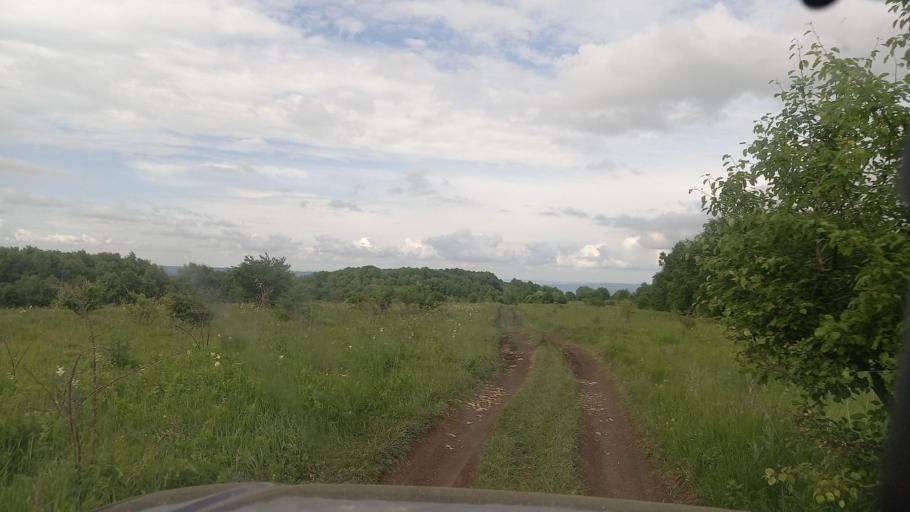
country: RU
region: Karachayevo-Cherkesiya
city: Pregradnaya
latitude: 44.0314
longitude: 41.3087
